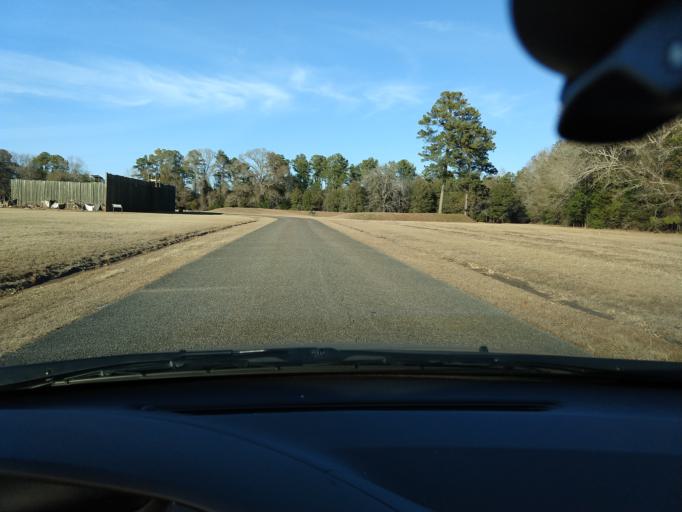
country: US
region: Georgia
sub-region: Macon County
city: Oglethorpe
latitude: 32.1952
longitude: -84.1270
